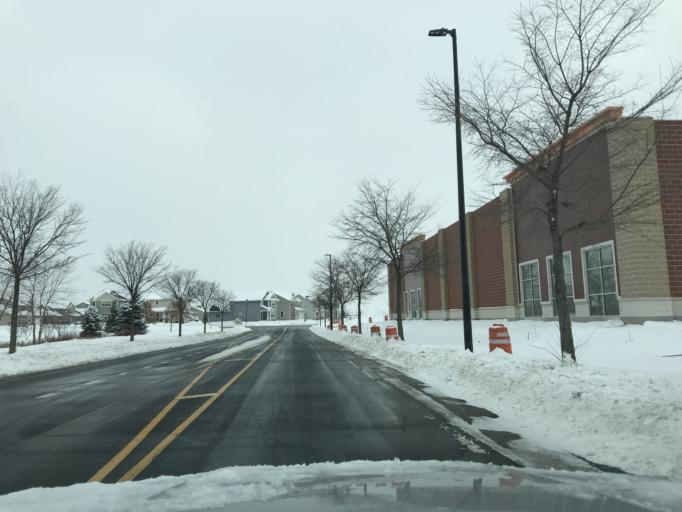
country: US
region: Wisconsin
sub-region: Dane County
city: Sun Prairie
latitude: 43.1706
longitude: -89.2708
